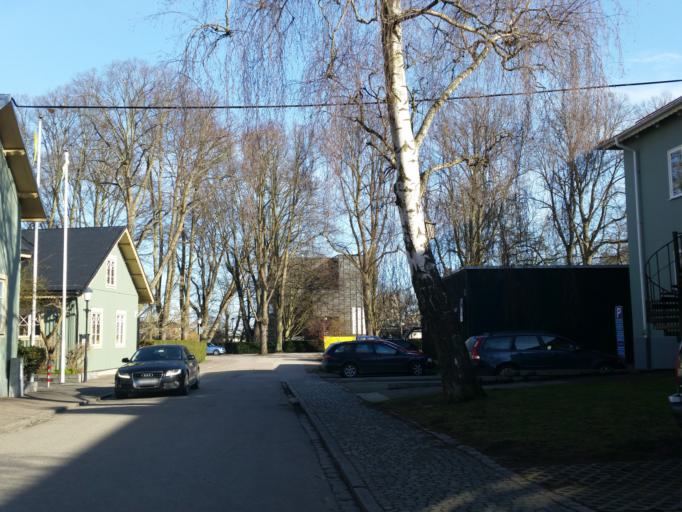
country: SE
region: Kalmar
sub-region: Kalmar Kommun
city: Kalmar
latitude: 56.6613
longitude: 16.3537
